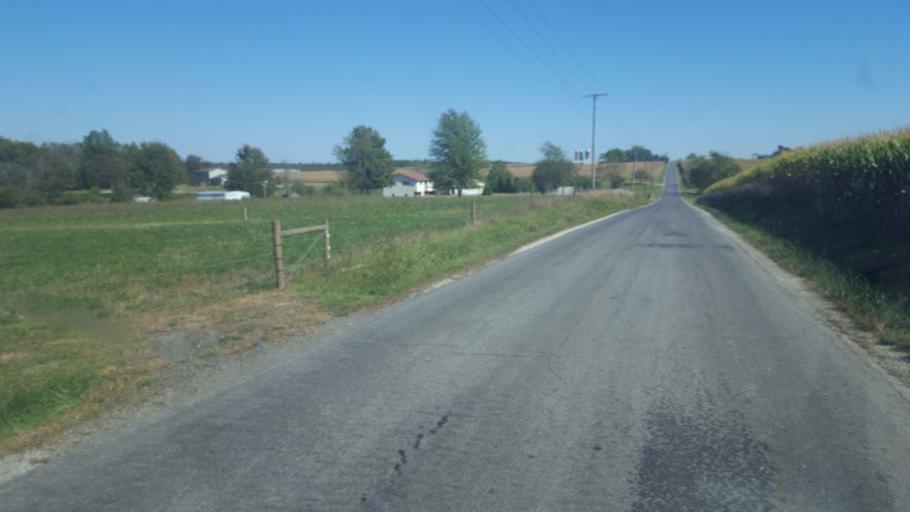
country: US
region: Ohio
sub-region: Huron County
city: Greenwich
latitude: 40.9940
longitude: -82.5677
